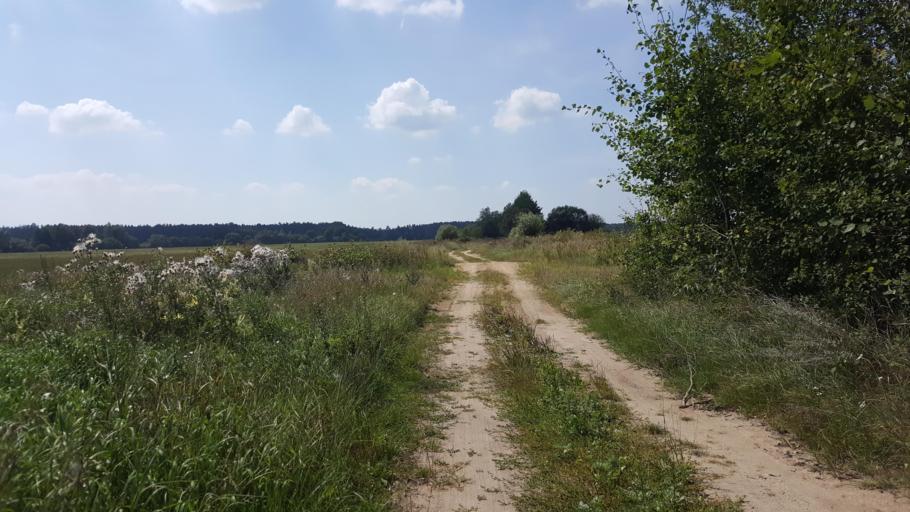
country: PL
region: Podlasie
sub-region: Powiat hajnowski
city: Hajnowka
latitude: 52.5786
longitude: 23.5725
